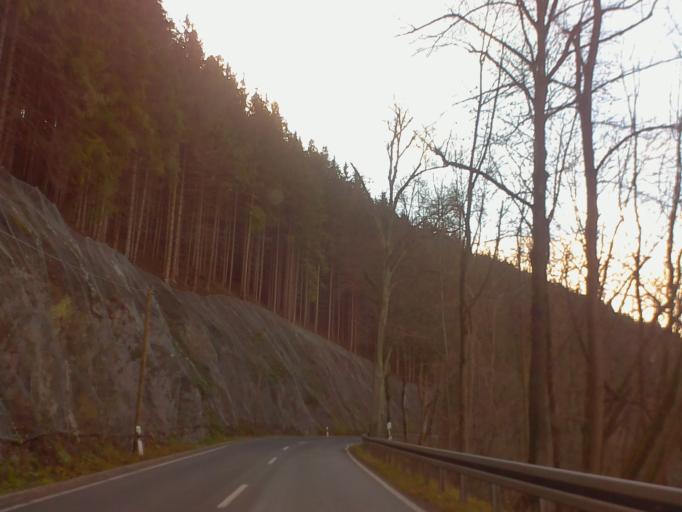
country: DE
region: Thuringia
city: Meuselbach
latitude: 50.5801
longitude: 11.0792
